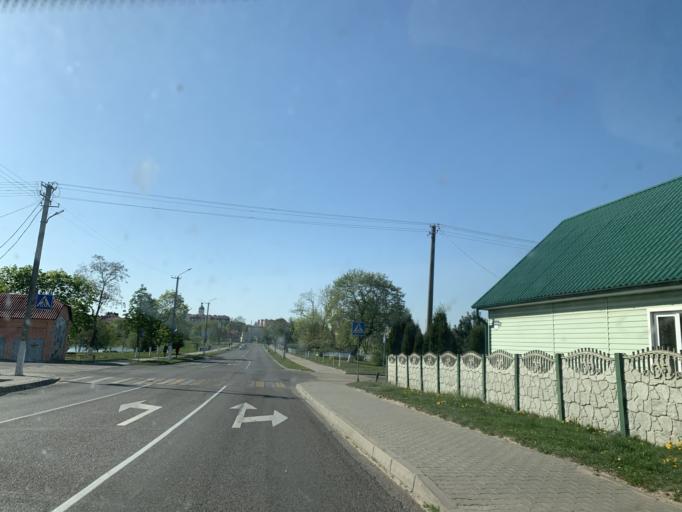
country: BY
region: Minsk
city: Nyasvizh
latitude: 53.2162
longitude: 26.6897
